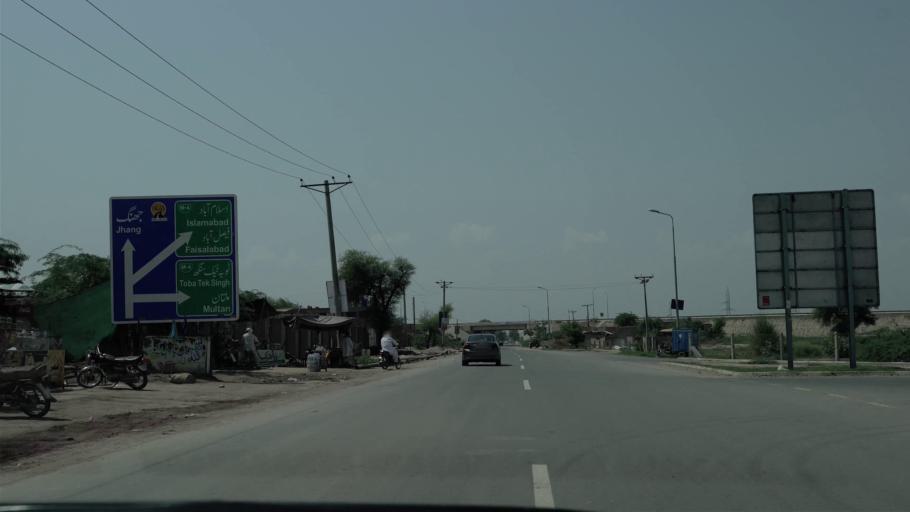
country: PK
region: Punjab
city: Gojra
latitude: 31.1782
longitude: 72.6328
